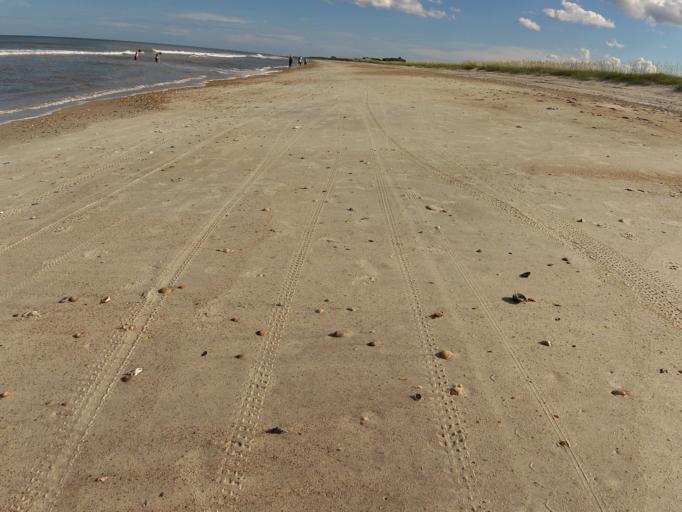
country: US
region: Florida
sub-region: Nassau County
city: Fernandina Beach
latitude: 30.6958
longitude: -81.4277
